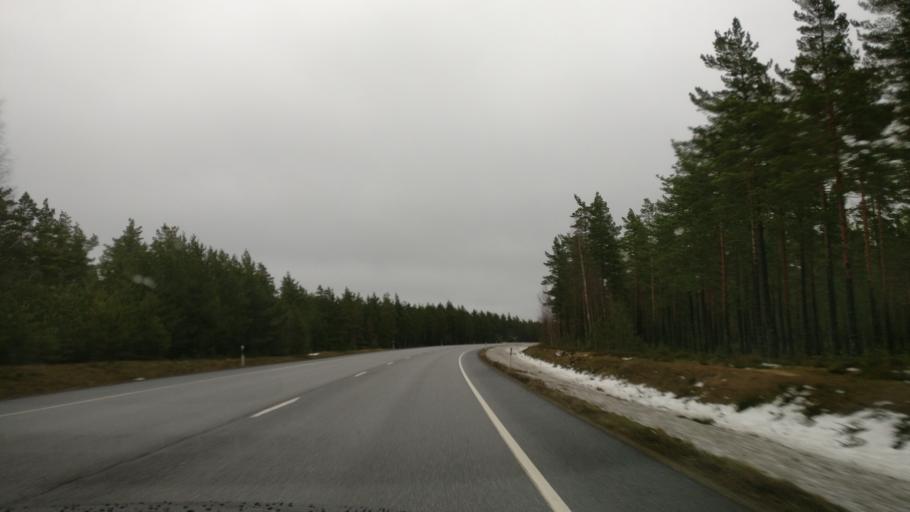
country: FI
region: Uusimaa
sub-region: Raaseporin
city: Hanko
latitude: 59.8593
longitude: 23.0314
